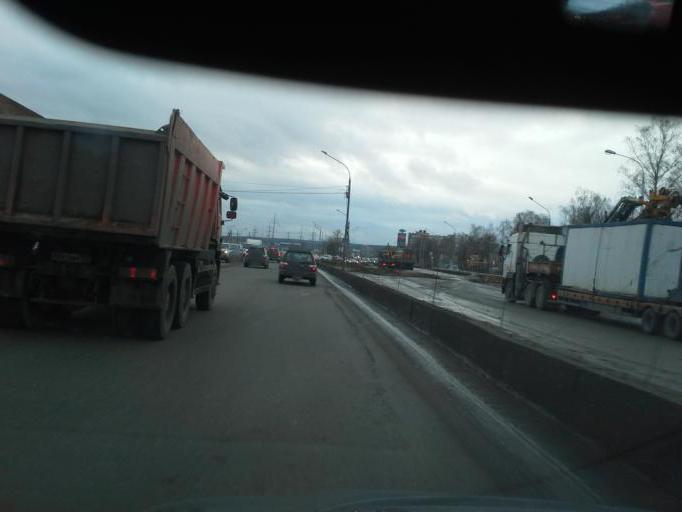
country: RU
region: Moskovskaya
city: Kommunarka
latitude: 55.5732
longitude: 37.4561
